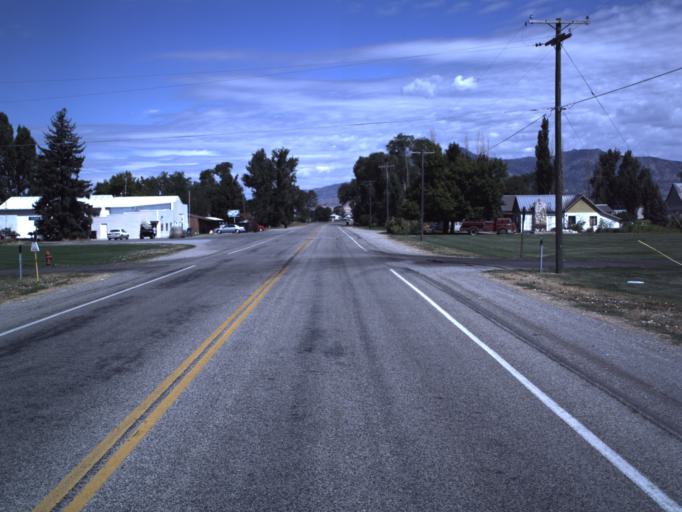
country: US
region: Utah
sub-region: Box Elder County
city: Garland
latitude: 41.7885
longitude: -112.1494
